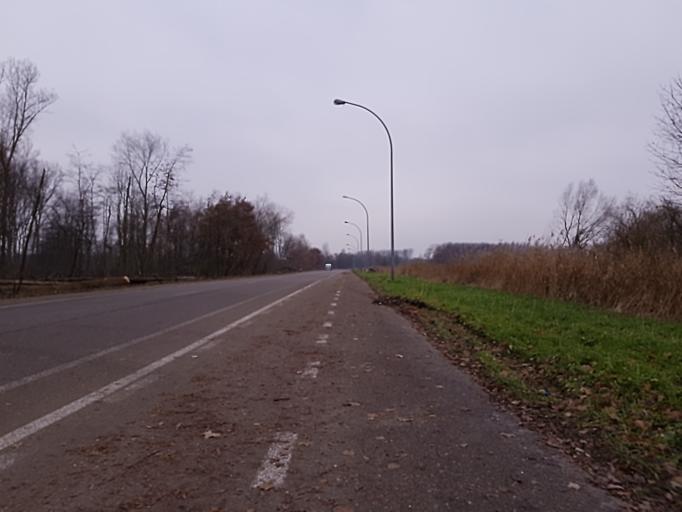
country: BE
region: Flanders
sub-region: Provincie Antwerpen
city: Boom
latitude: 51.0707
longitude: 4.3907
